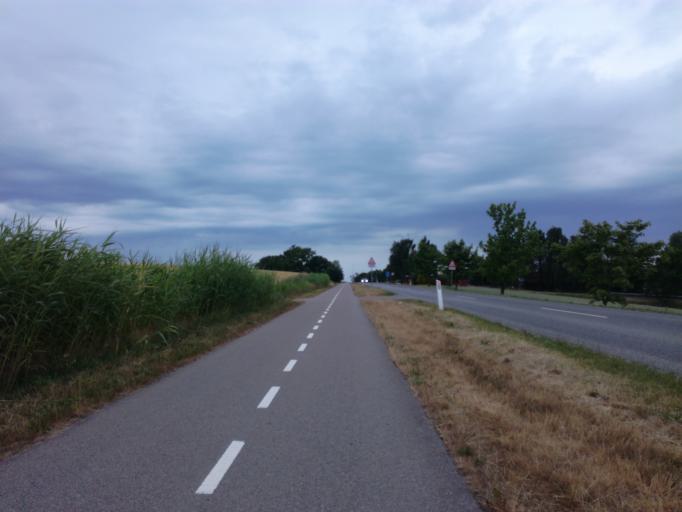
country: DK
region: South Denmark
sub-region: Vejle Kommune
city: Borkop
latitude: 55.6616
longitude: 9.6300
